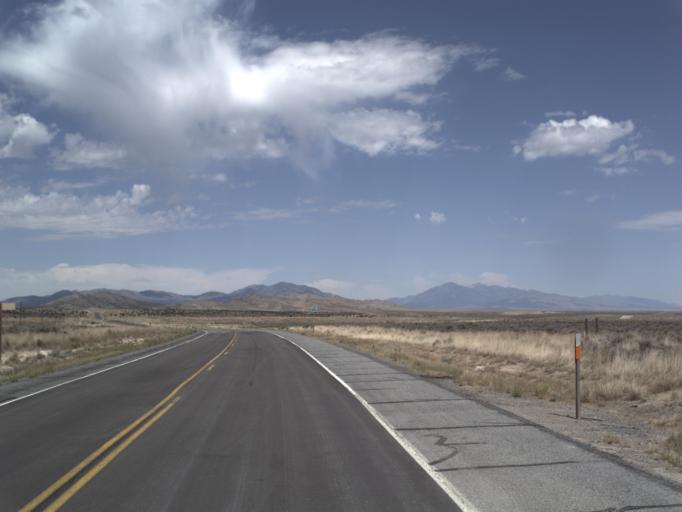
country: US
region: Utah
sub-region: Utah County
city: Eagle Mountain
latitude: 40.0514
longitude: -112.2969
